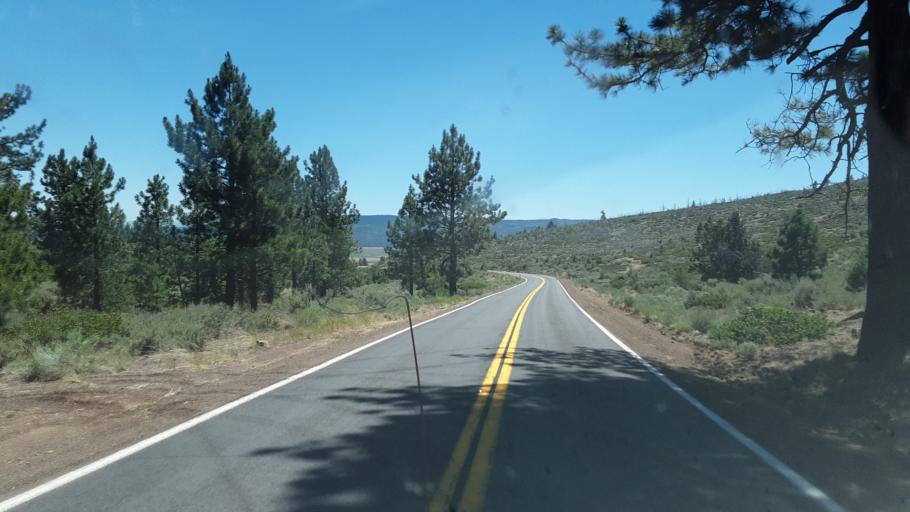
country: US
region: California
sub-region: Lassen County
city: Susanville
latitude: 40.6120
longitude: -120.6433
